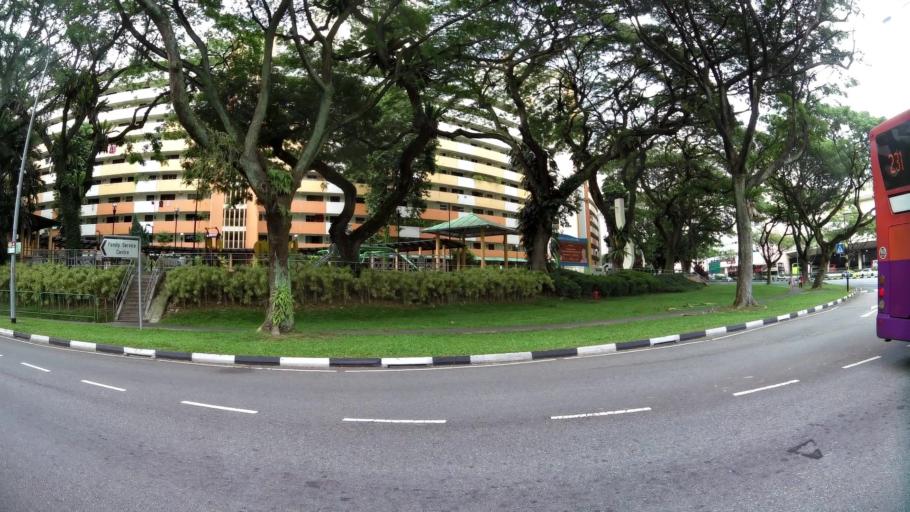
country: SG
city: Singapore
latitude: 1.3317
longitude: 103.8458
